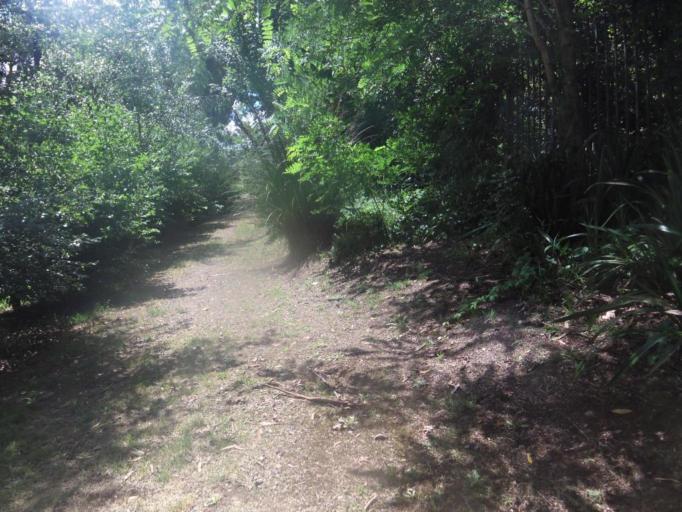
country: AU
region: Victoria
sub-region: Yarra Ranges
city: Millgrove
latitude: -37.5120
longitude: 145.7533
